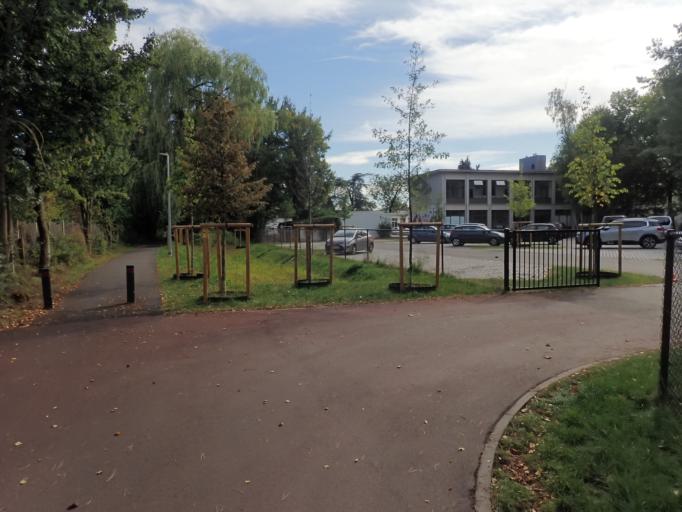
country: BE
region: Flanders
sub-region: Provincie Antwerpen
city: Kalmthout
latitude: 51.3789
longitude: 4.4723
